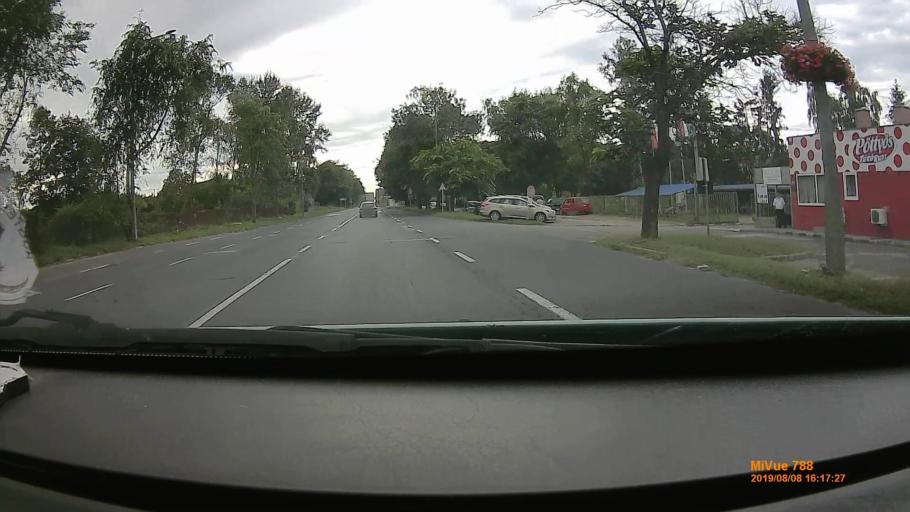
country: HU
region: Szabolcs-Szatmar-Bereg
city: Mateszalka
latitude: 47.9632
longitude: 22.2941
